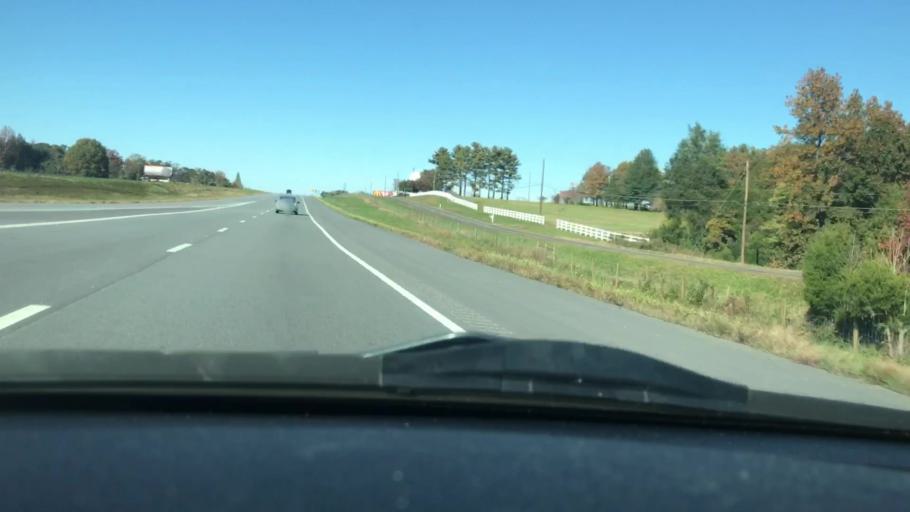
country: US
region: North Carolina
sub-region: Guilford County
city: Stokesdale
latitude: 36.2862
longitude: -79.9395
